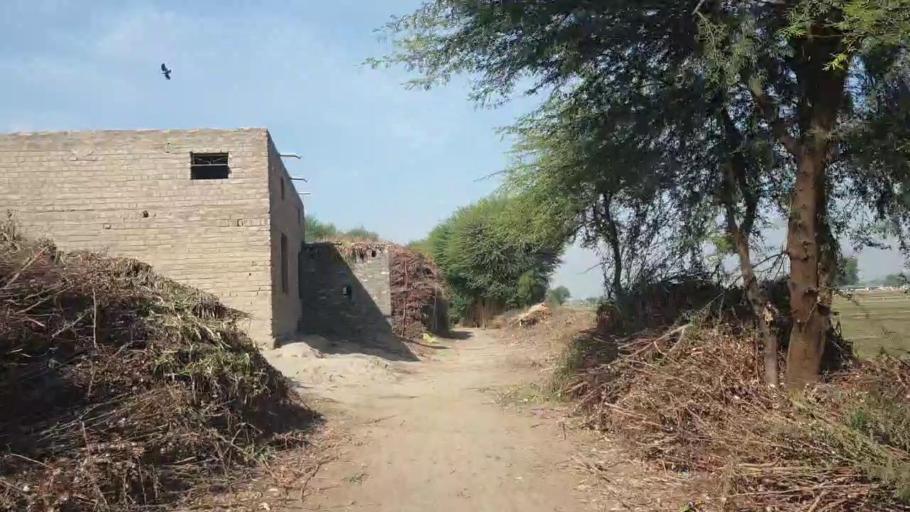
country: PK
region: Sindh
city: Matiari
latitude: 25.6800
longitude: 68.3465
